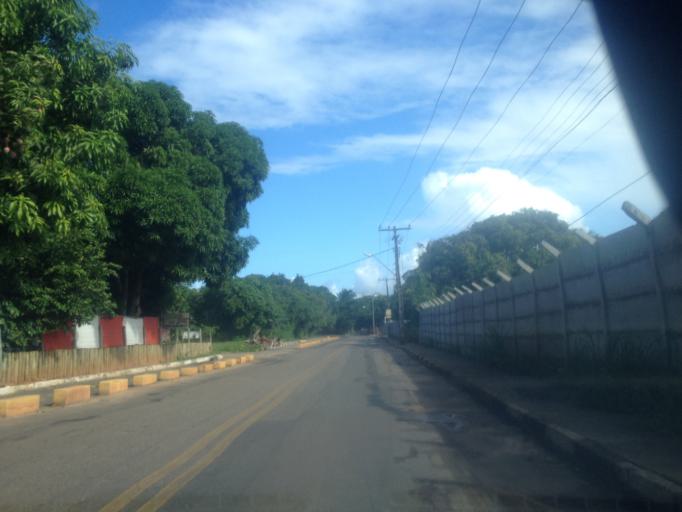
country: BR
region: Bahia
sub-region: Mata De Sao Joao
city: Mata de Sao Joao
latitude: -12.6007
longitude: -38.0403
